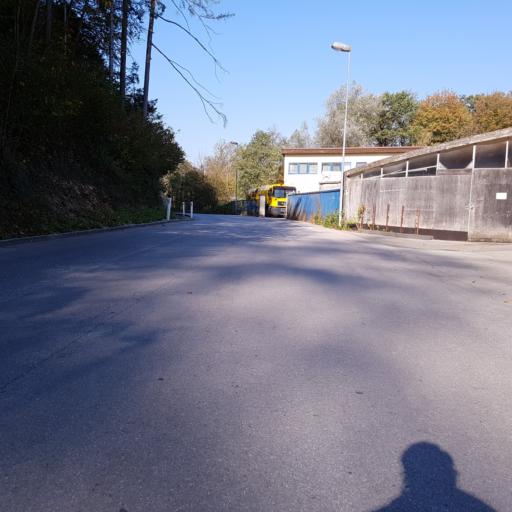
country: AT
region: Salzburg
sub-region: Politischer Bezirk Hallein
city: Hallein
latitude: 47.6697
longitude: 13.1066
